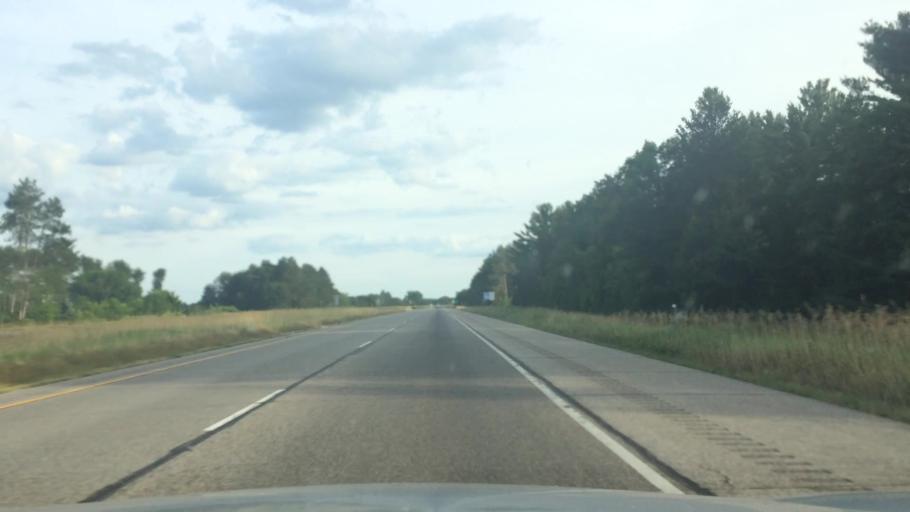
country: US
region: Wisconsin
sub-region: Portage County
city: Plover
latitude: 44.2069
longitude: -89.5240
